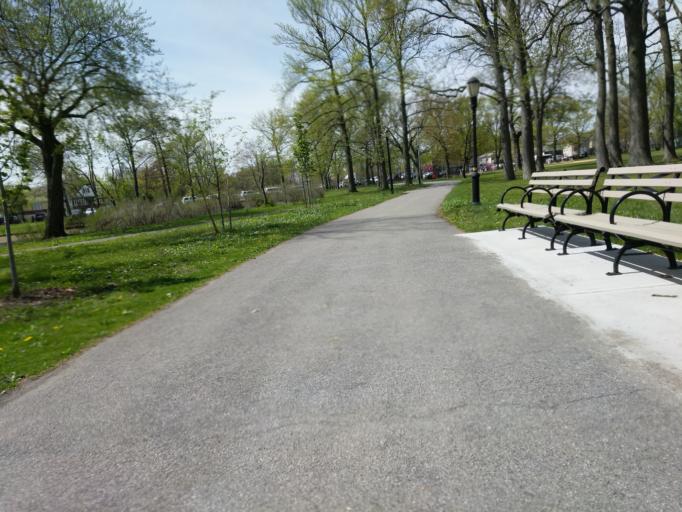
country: US
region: New York
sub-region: Nassau County
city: South Valley Stream
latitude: 40.6587
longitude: -73.7465
